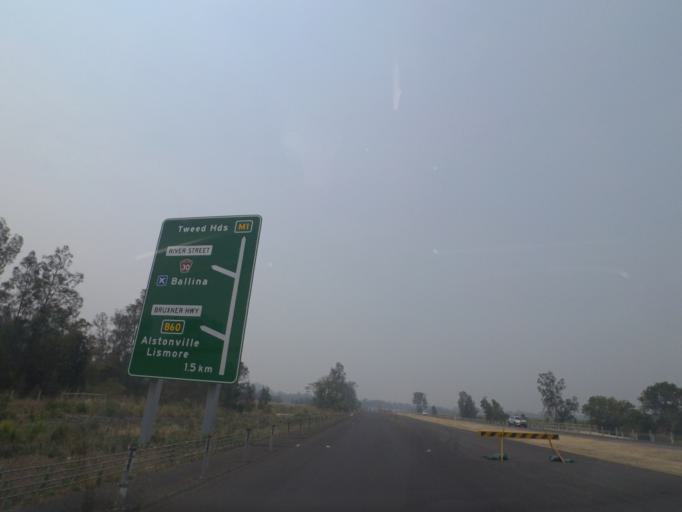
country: AU
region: New South Wales
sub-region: Ballina
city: Ballina
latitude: -28.8758
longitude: 153.4888
